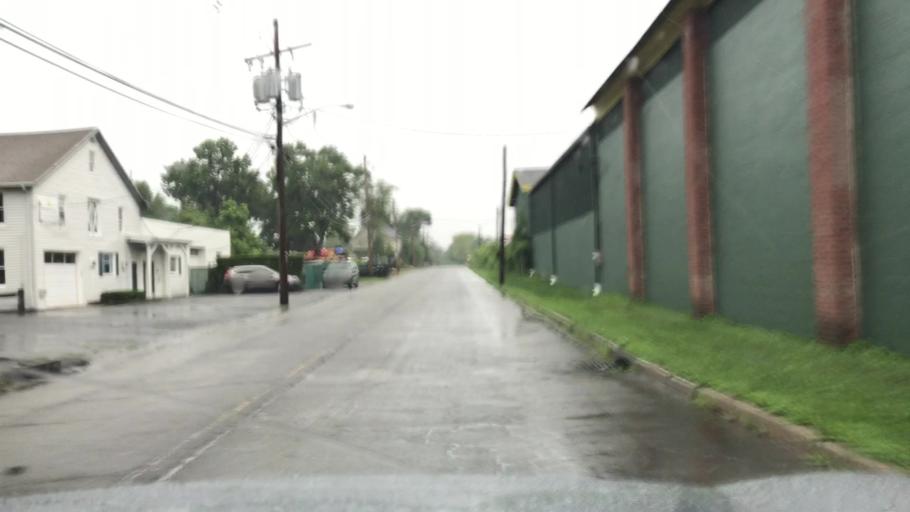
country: US
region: New Jersey
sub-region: Bergen County
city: Closter
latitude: 40.9752
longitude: -73.9613
